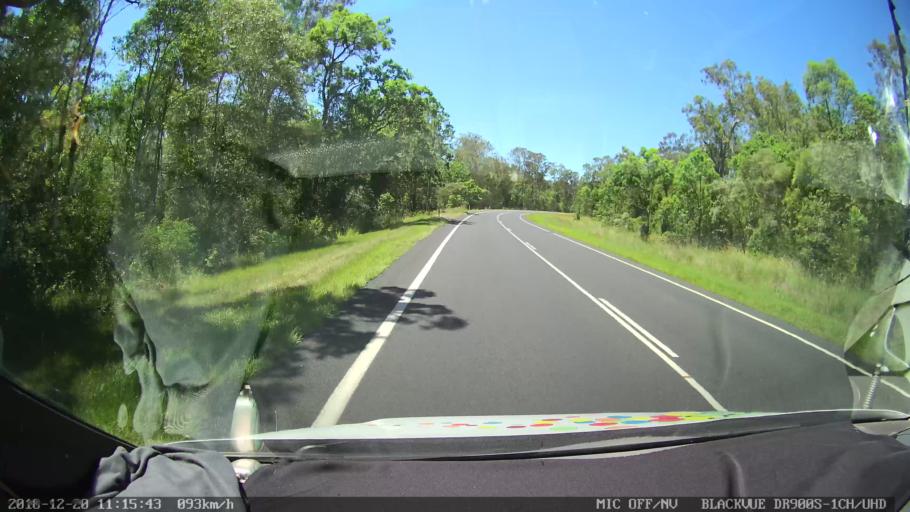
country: AU
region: New South Wales
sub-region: Richmond Valley
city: Casino
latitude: -29.0168
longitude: 153.0105
